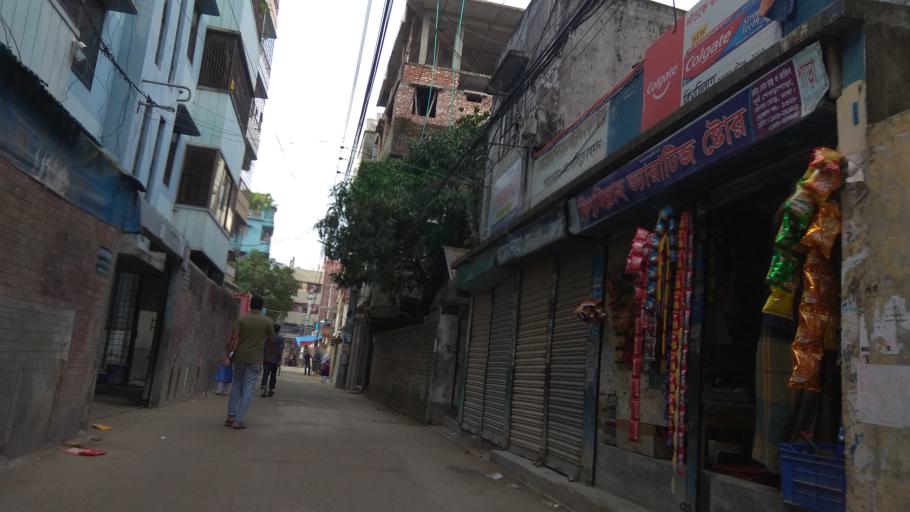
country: BD
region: Dhaka
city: Azimpur
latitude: 23.7937
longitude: 90.3791
